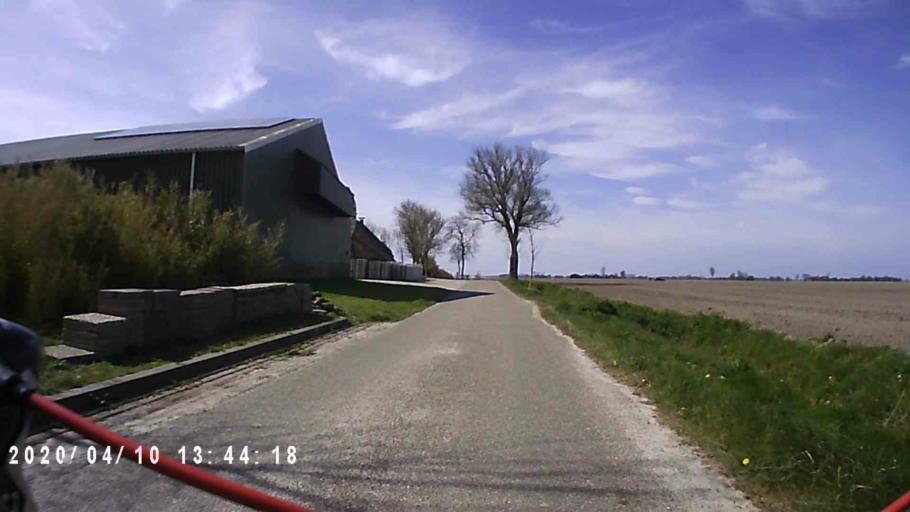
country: NL
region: Groningen
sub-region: Gemeente De Marne
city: Ulrum
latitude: 53.3745
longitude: 6.3784
